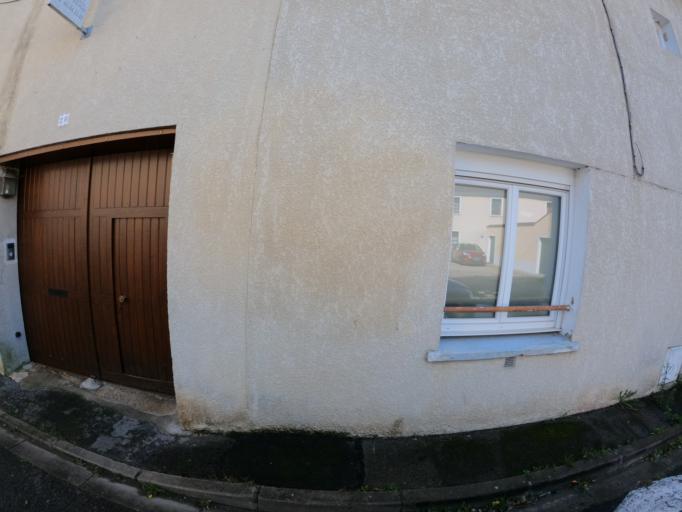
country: FR
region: Ile-de-France
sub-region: Departement de Seine-et-Marne
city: Saint-Germain-sur-Morin
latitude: 48.8813
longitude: 2.8535
